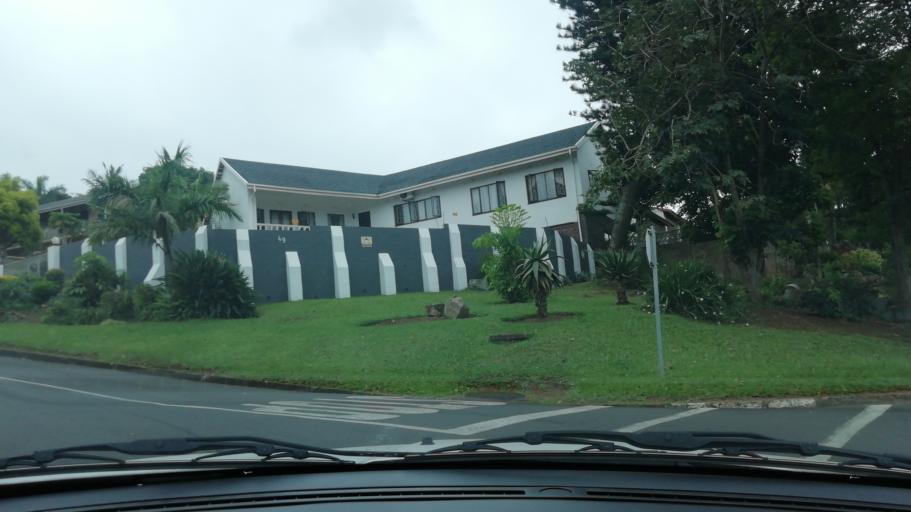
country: ZA
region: KwaZulu-Natal
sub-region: uThungulu District Municipality
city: Empangeni
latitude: -28.7567
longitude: 31.8914
